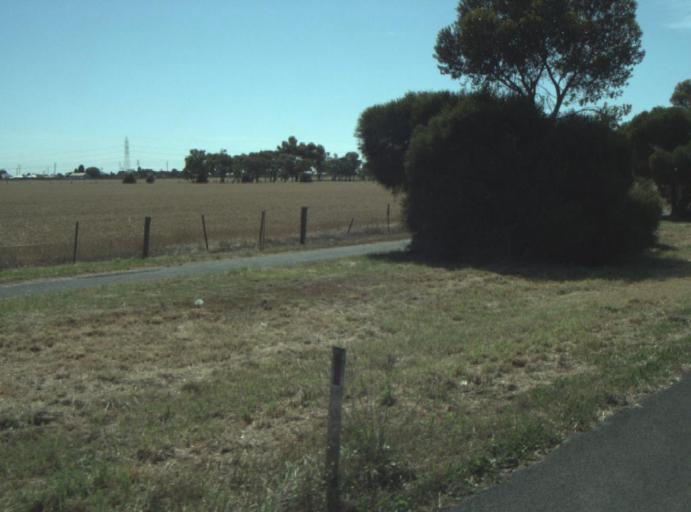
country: AU
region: Victoria
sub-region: Greater Geelong
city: Bell Post Hill
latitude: -38.1014
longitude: 144.3132
